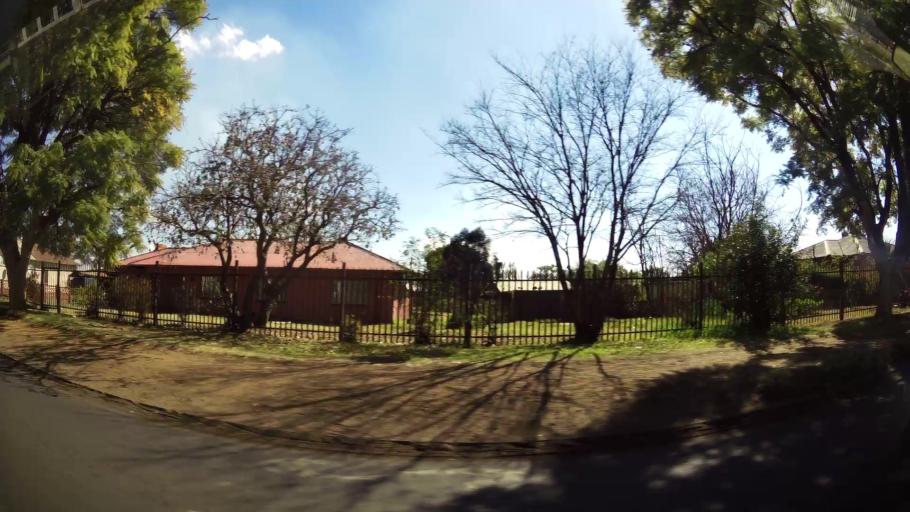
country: ZA
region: Mpumalanga
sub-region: Nkangala District Municipality
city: Witbank
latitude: -25.8689
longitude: 29.2146
